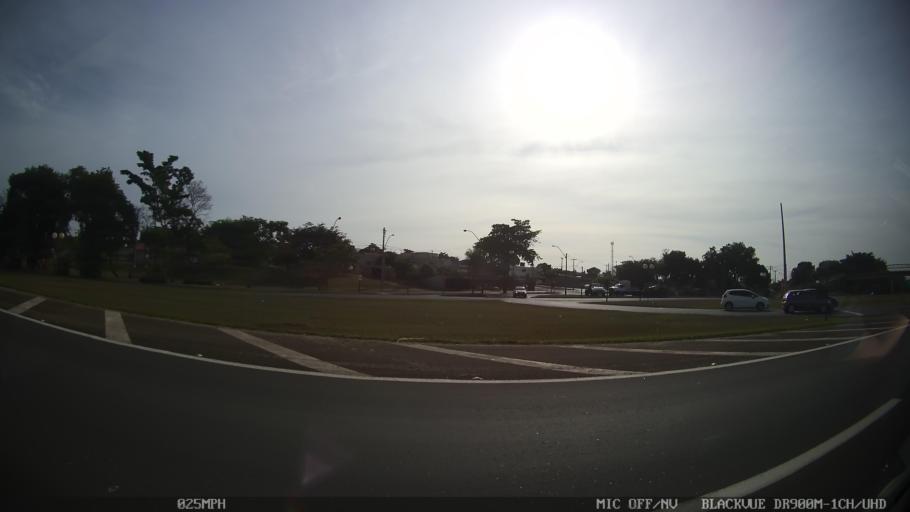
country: BR
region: Sao Paulo
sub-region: Piracicaba
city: Piracicaba
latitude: -22.6800
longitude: -47.7043
